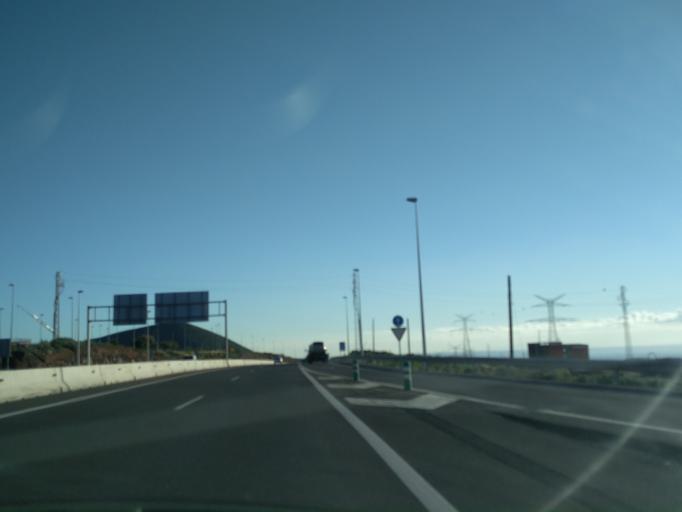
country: ES
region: Canary Islands
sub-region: Provincia de Santa Cruz de Tenerife
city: San Isidro
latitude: 28.0712
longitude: -16.5533
